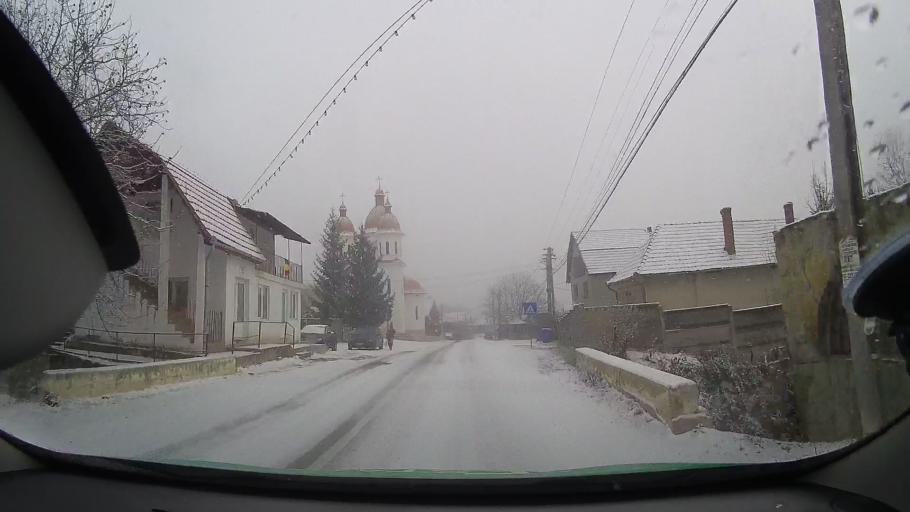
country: RO
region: Alba
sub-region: Comuna Livezile
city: Livezile
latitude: 46.3492
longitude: 23.6295
